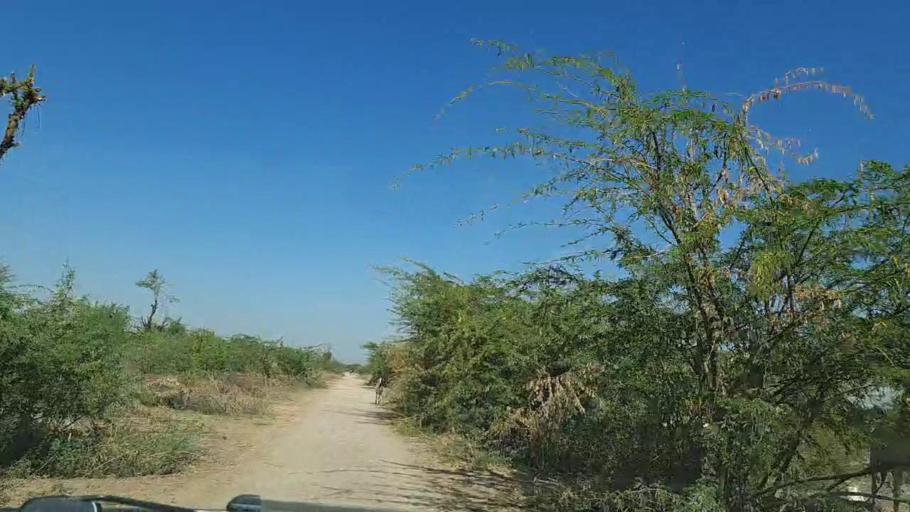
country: PK
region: Sindh
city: Dhoro Naro
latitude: 25.4618
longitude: 69.5136
